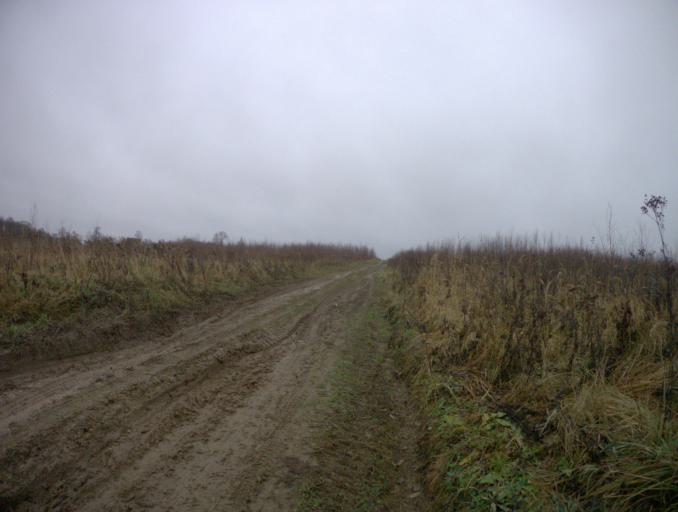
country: RU
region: Vladimir
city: Golovino
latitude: 55.9852
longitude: 40.4471
